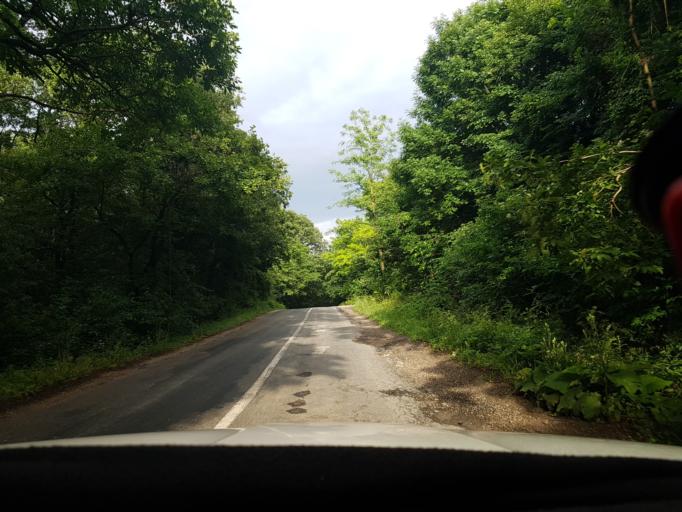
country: HU
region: Komarom-Esztergom
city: Nyergesujfalu
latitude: 47.7238
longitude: 18.5425
